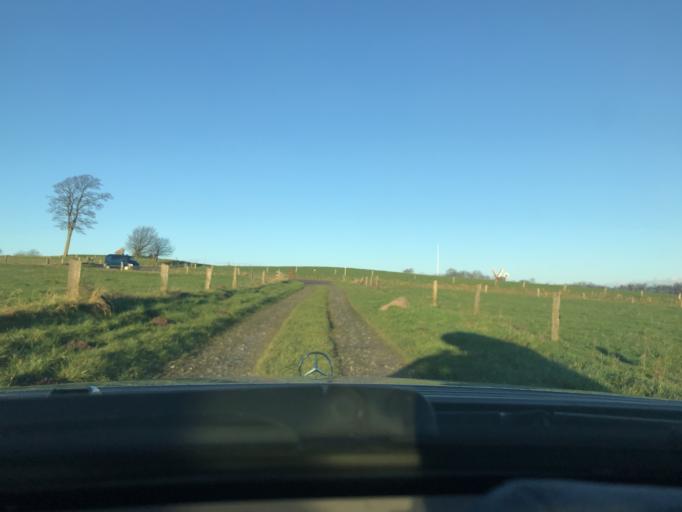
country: DK
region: South Denmark
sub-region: Sonderborg Kommune
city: Dybbol
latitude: 54.9036
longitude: 9.7538
